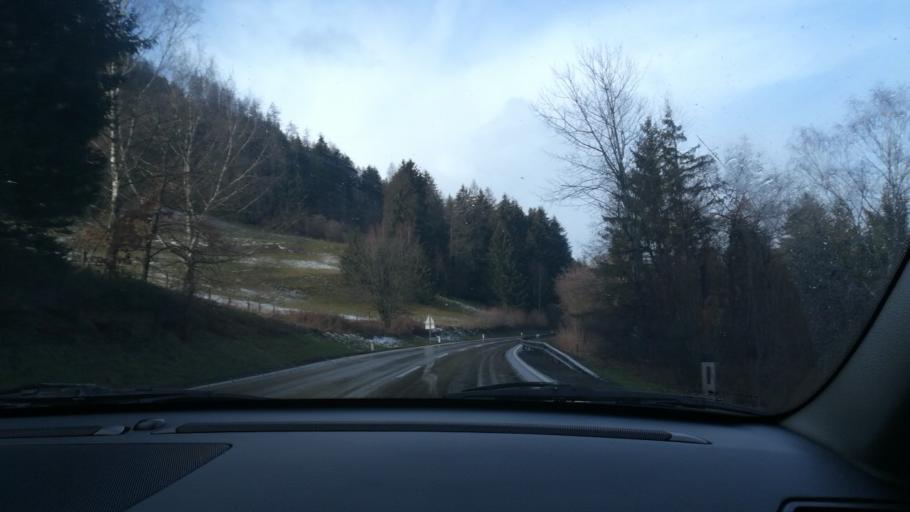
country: AT
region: Styria
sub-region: Politischer Bezirk Murtal
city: Sankt Peter ob Judenburg
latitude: 47.1938
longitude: 14.5792
